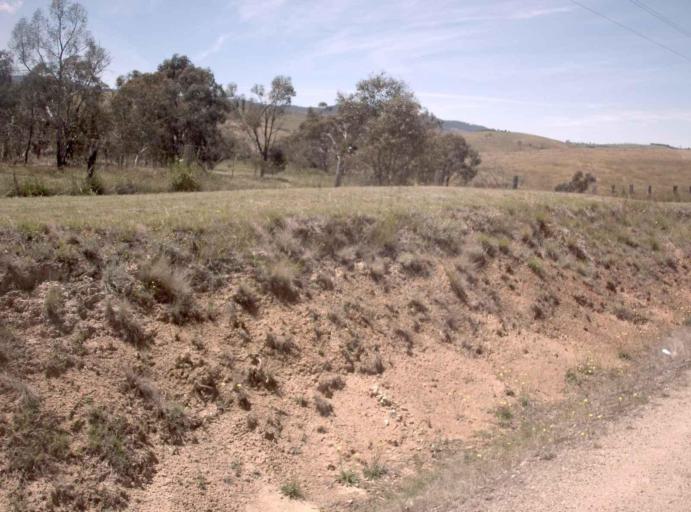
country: AU
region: Victoria
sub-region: Alpine
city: Mount Beauty
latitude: -37.1017
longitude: 147.6016
